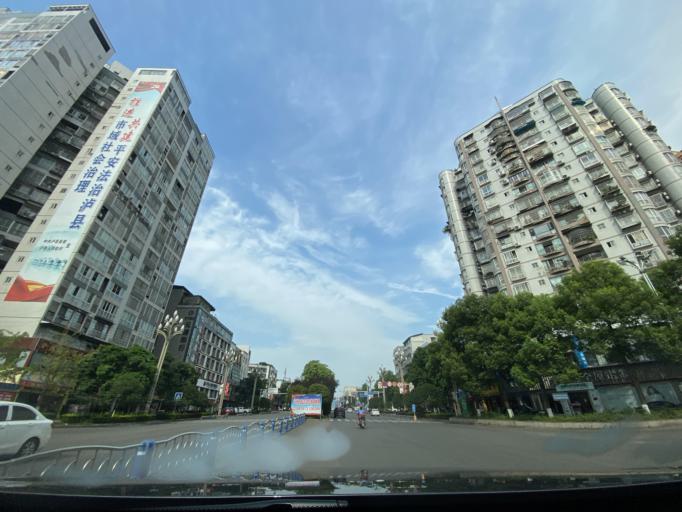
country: CN
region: Sichuan
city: Fuji
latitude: 29.1538
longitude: 105.3638
